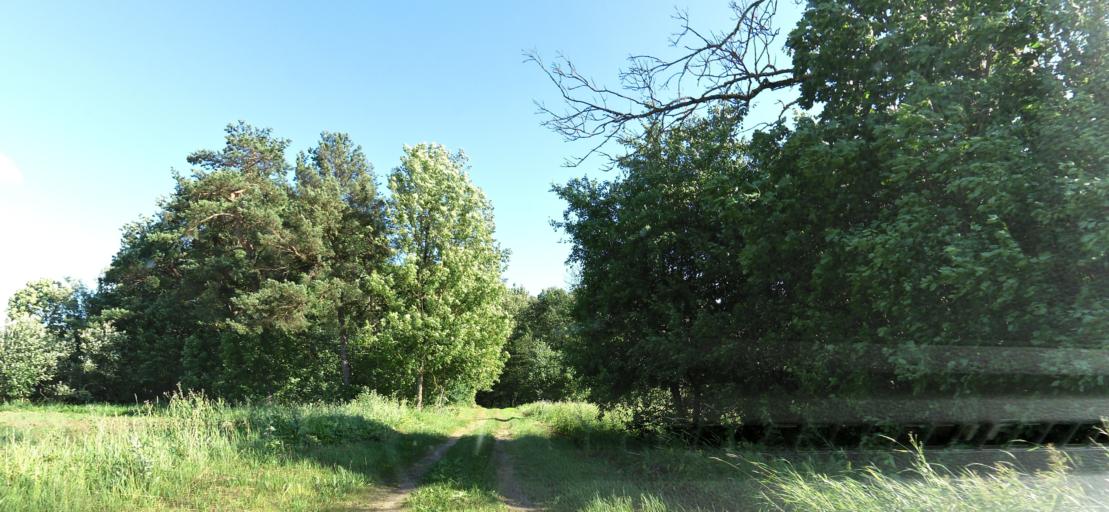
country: LT
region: Panevezys
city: Pasvalys
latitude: 56.1486
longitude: 24.4567
